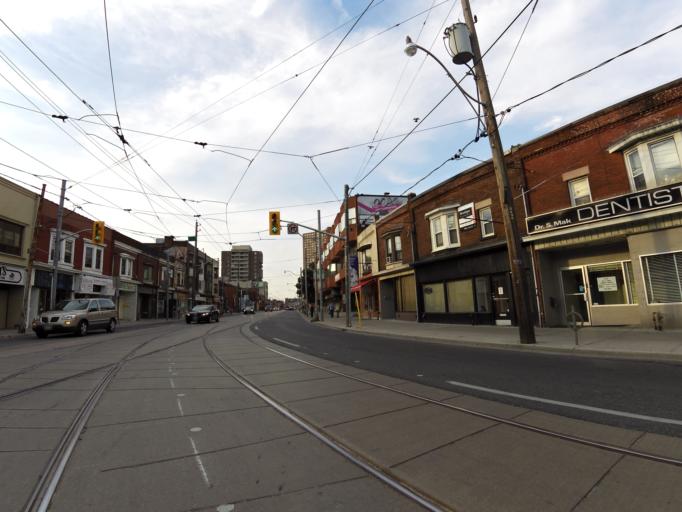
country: CA
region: Ontario
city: Toronto
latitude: 43.6538
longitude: -79.4517
